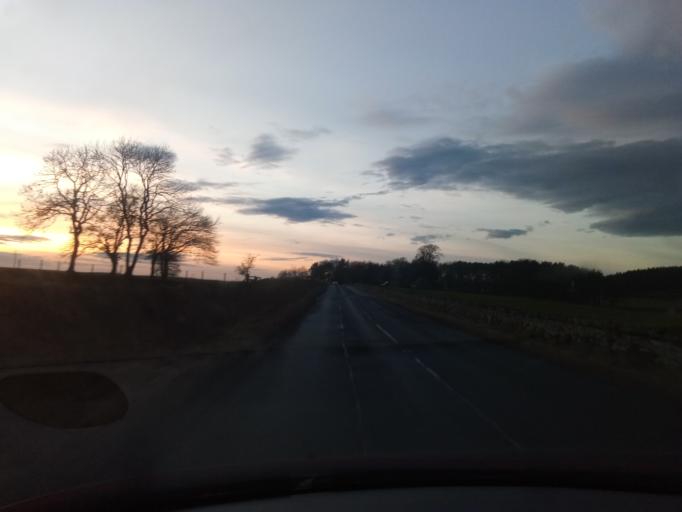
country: GB
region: England
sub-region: Northumberland
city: Otterburn
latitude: 55.2317
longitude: -2.1399
